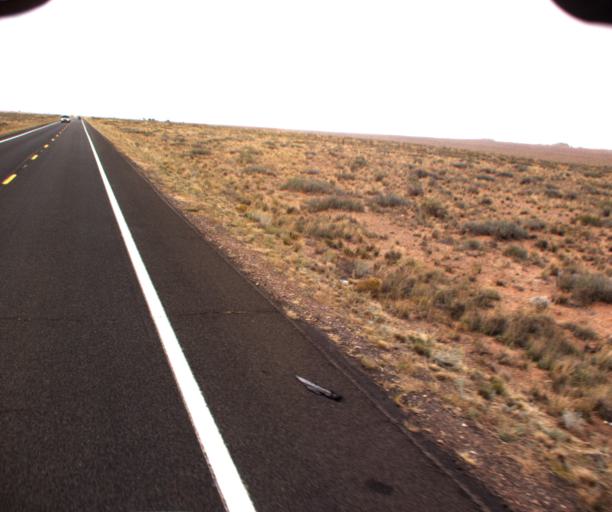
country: US
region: Arizona
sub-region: Coconino County
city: Tuba City
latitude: 36.1592
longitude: -111.1103
